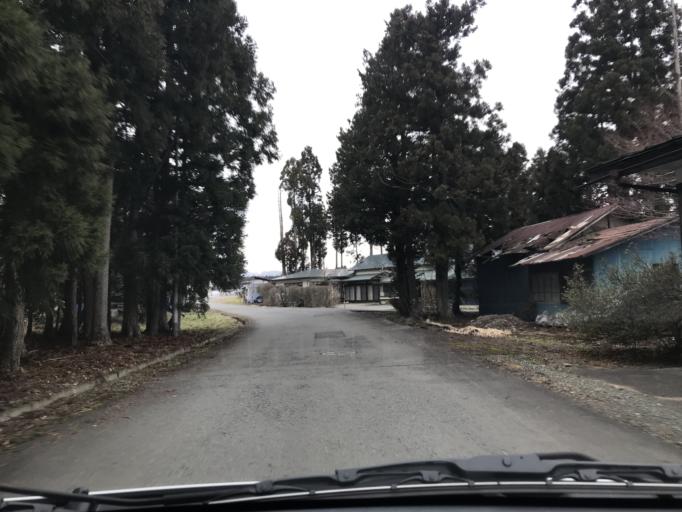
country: JP
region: Iwate
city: Kitakami
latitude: 39.2176
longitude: 141.0720
